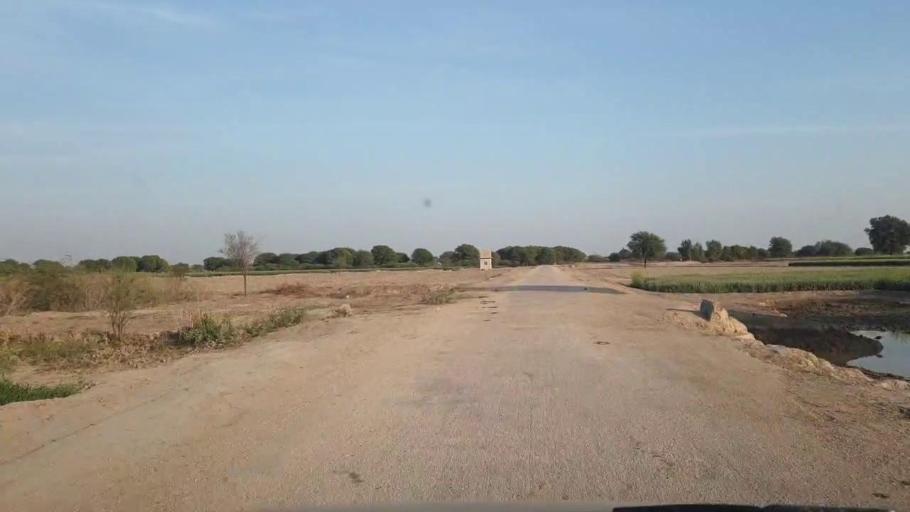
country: PK
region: Sindh
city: Chambar
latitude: 25.2600
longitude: 68.8012
